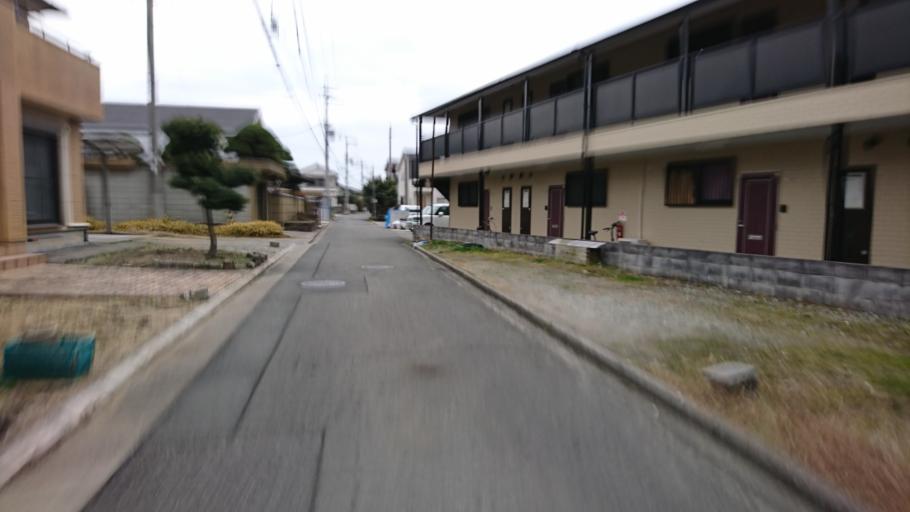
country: JP
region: Hyogo
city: Kakogawacho-honmachi
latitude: 34.7460
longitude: 134.8585
